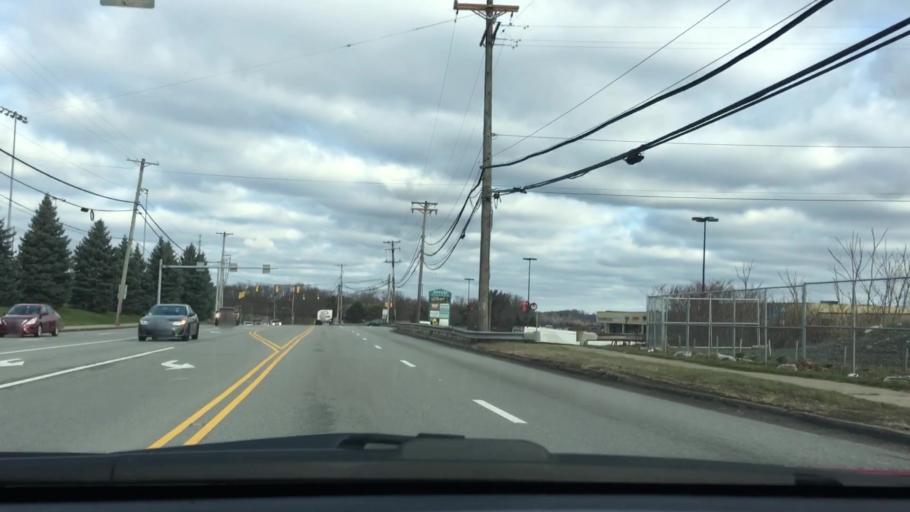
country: US
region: Pennsylvania
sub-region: Allegheny County
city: Monroeville
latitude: 40.4307
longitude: -79.7513
